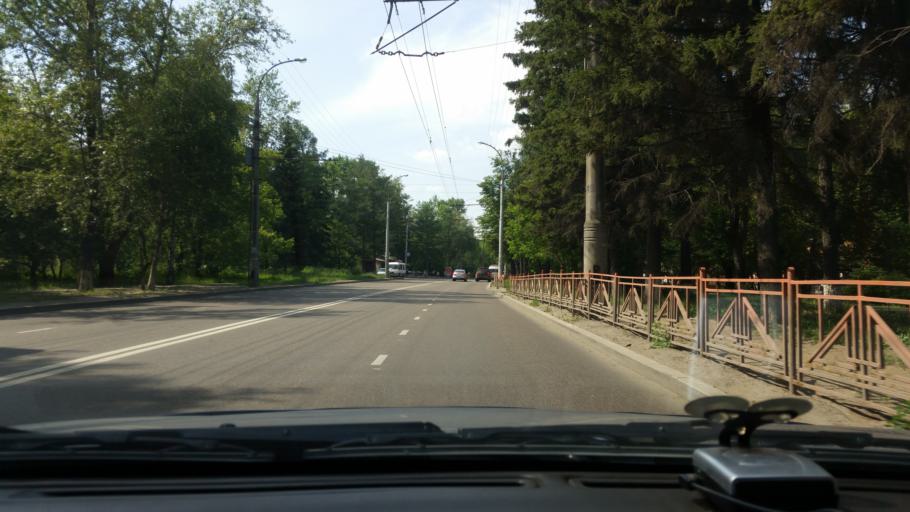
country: RU
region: Irkutsk
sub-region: Irkutskiy Rayon
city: Irkutsk
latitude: 52.2414
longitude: 104.2741
